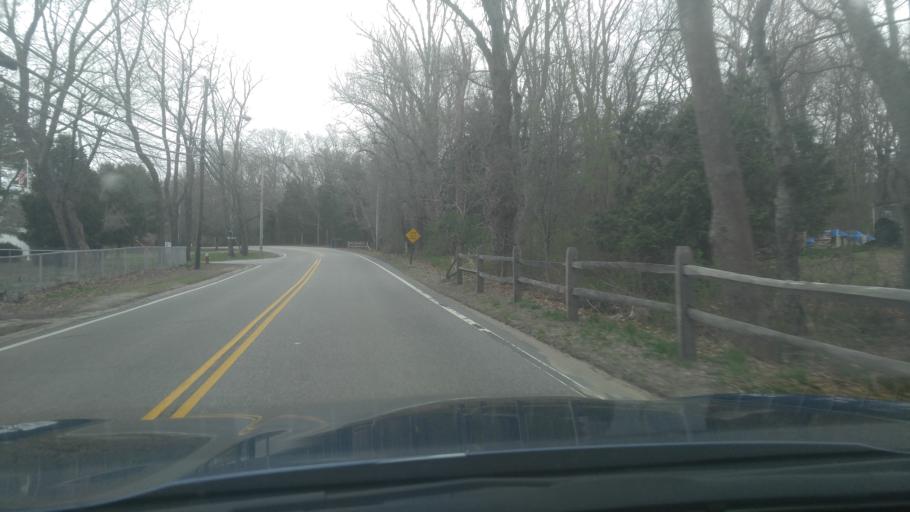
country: US
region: Rhode Island
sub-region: Washington County
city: North Kingstown
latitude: 41.5940
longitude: -71.4473
